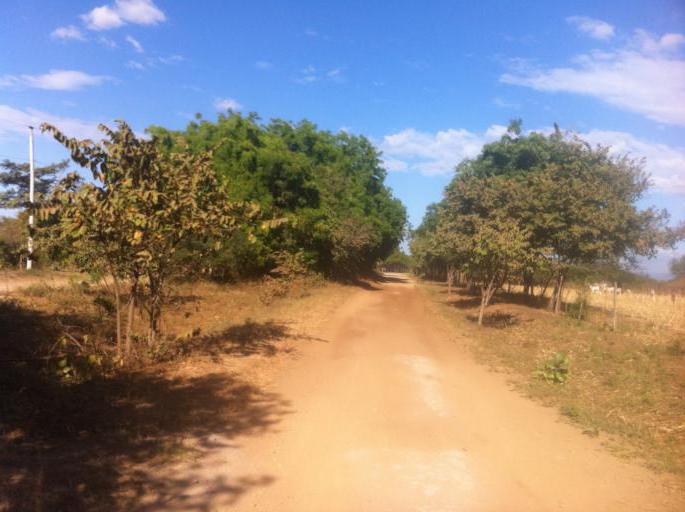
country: NI
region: Managua
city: Carlos Fonseca Amador
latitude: 11.9116
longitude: -86.6086
